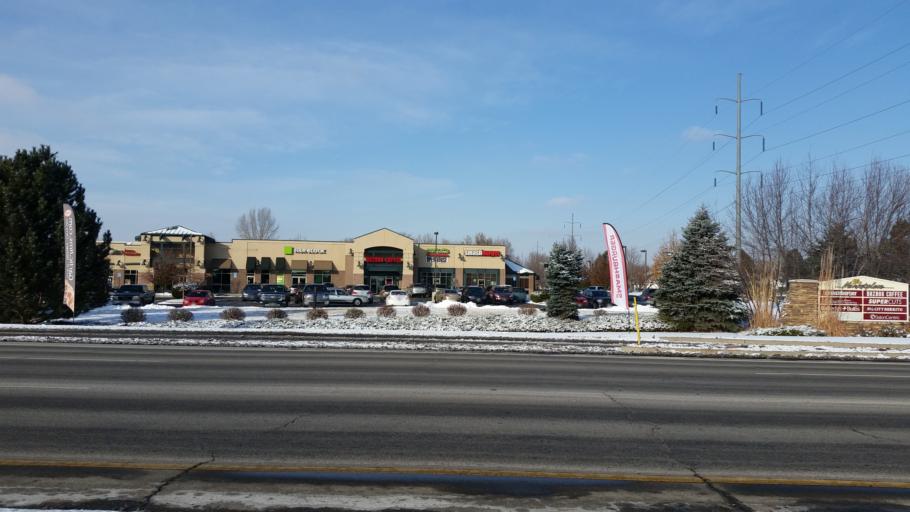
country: US
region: Colorado
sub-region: Larimer County
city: Loveland
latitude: 40.4073
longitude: -105.0452
